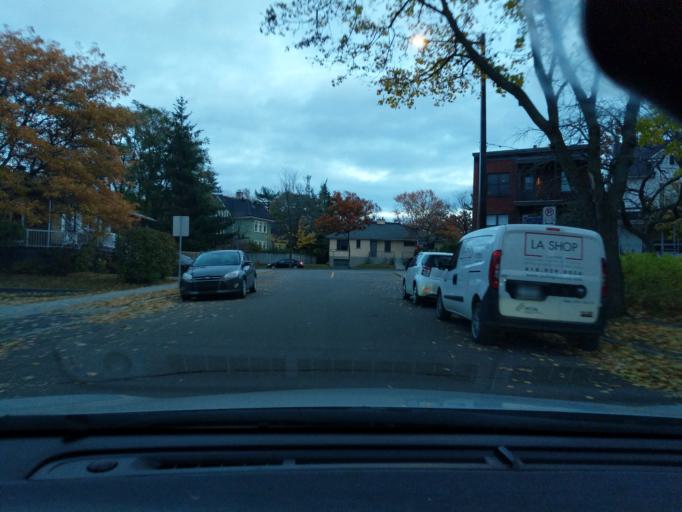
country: CA
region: Quebec
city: Quebec
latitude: 46.7884
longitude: -71.2493
